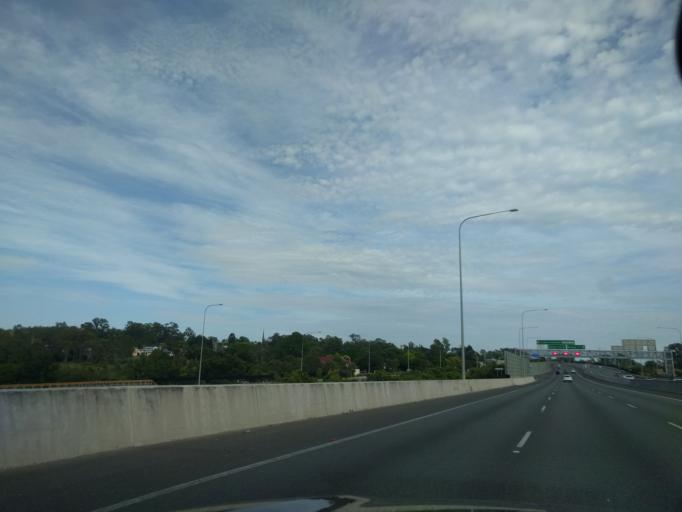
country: AU
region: Queensland
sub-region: Ipswich
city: Redbank
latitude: -27.6019
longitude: 152.8593
